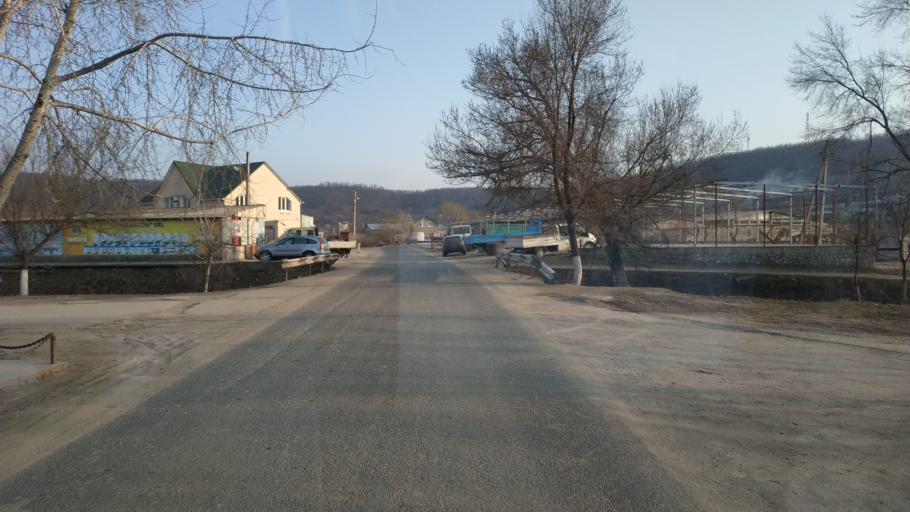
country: MD
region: Hincesti
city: Dancu
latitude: 46.7598
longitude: 28.3522
